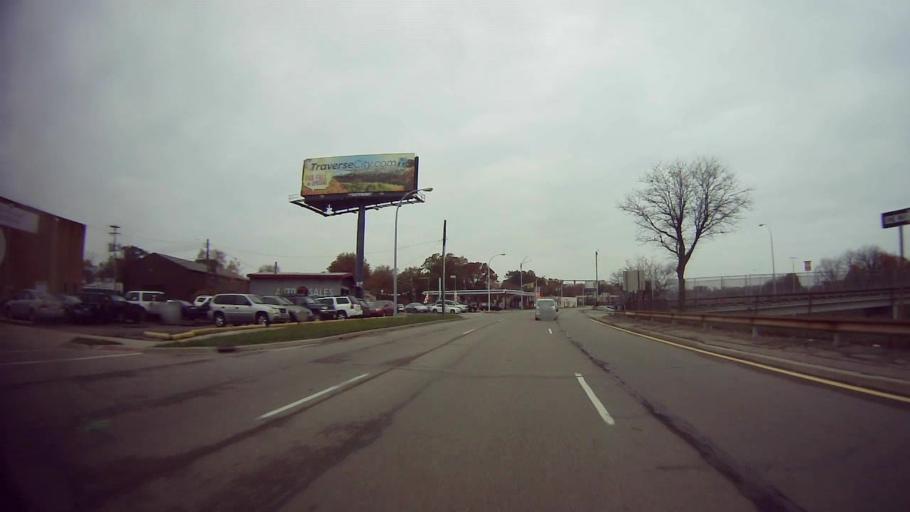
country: US
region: Michigan
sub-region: Oakland County
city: Hazel Park
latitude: 42.4584
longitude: -83.1026
